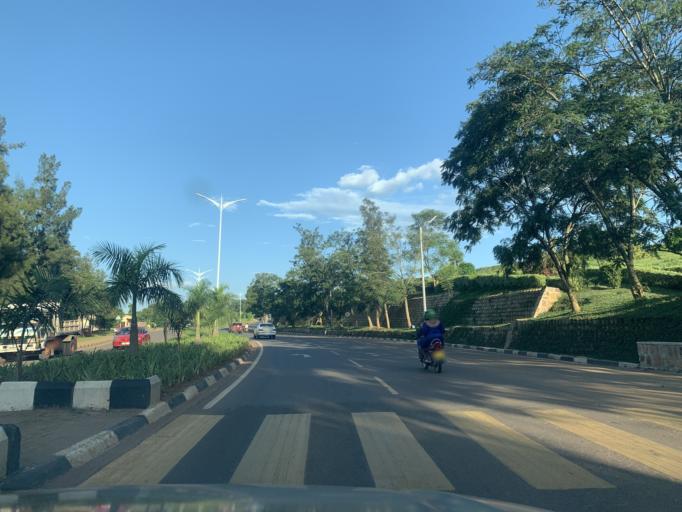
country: RW
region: Kigali
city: Kigali
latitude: -1.9637
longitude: 30.1276
